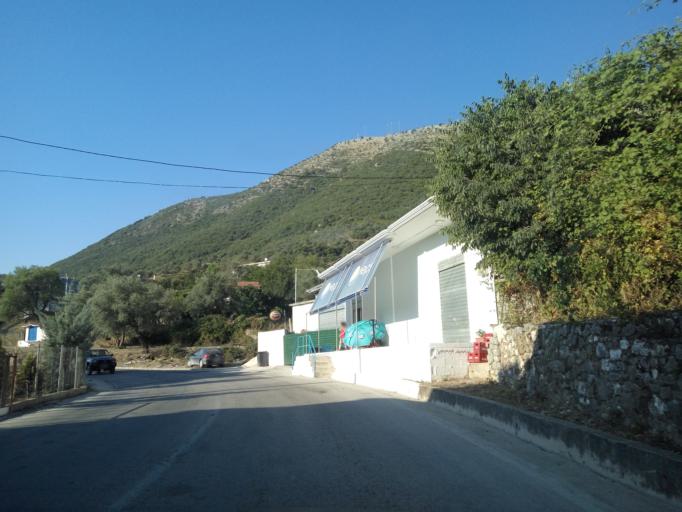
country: AL
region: Vlore
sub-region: Rrethi i Sarandes
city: Lukove
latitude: 39.9585
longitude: 19.9620
